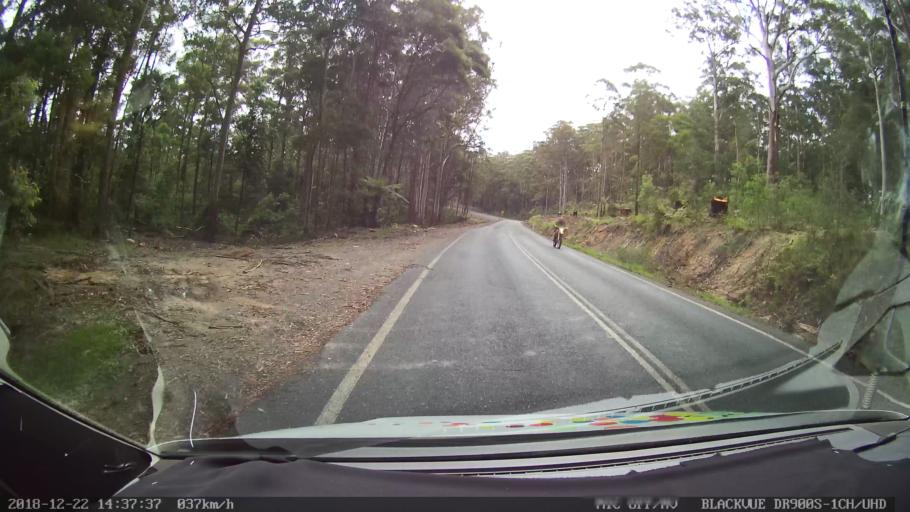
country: AU
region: New South Wales
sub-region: Bellingen
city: Dorrigo
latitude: -30.1336
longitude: 152.6005
